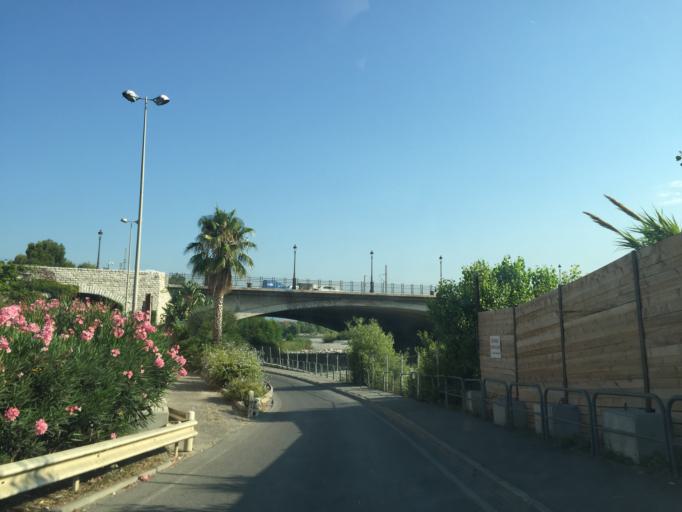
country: FR
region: Provence-Alpes-Cote d'Azur
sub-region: Departement des Alpes-Maritimes
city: Saint-Laurent-du-Var
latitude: 43.6626
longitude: 7.1980
